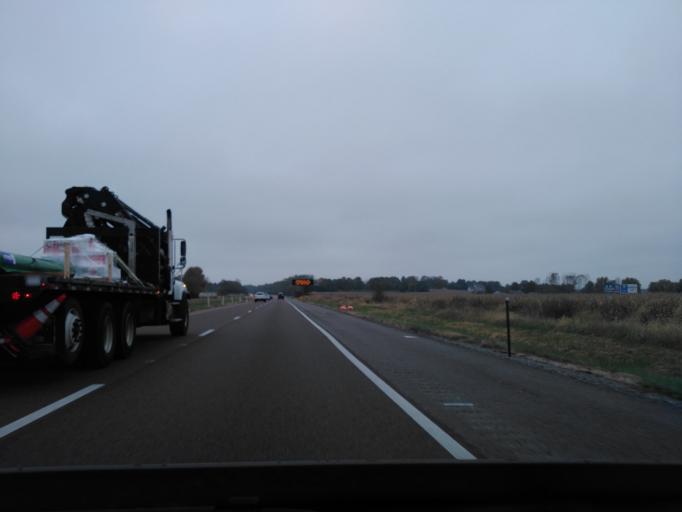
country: US
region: Illinois
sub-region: Madison County
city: Troy
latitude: 38.7557
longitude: -89.8650
